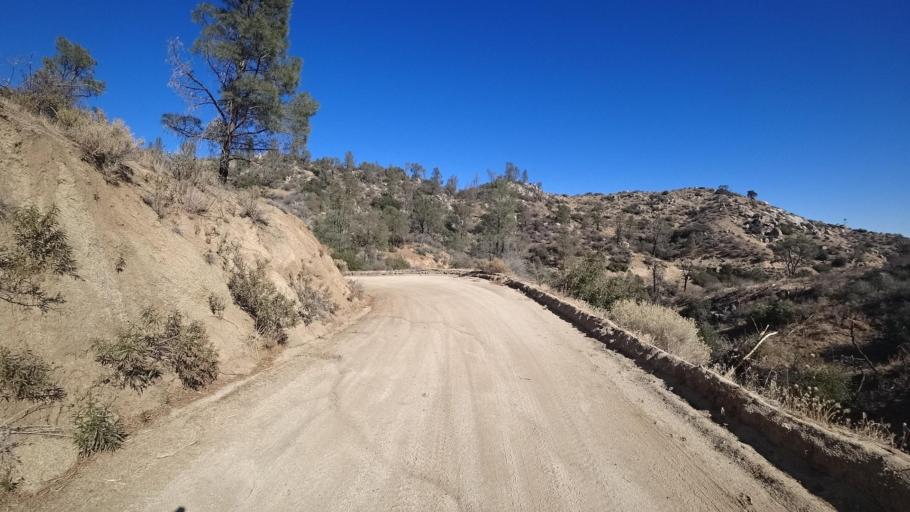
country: US
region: California
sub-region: Kern County
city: Wofford Heights
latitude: 35.7062
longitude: -118.4990
